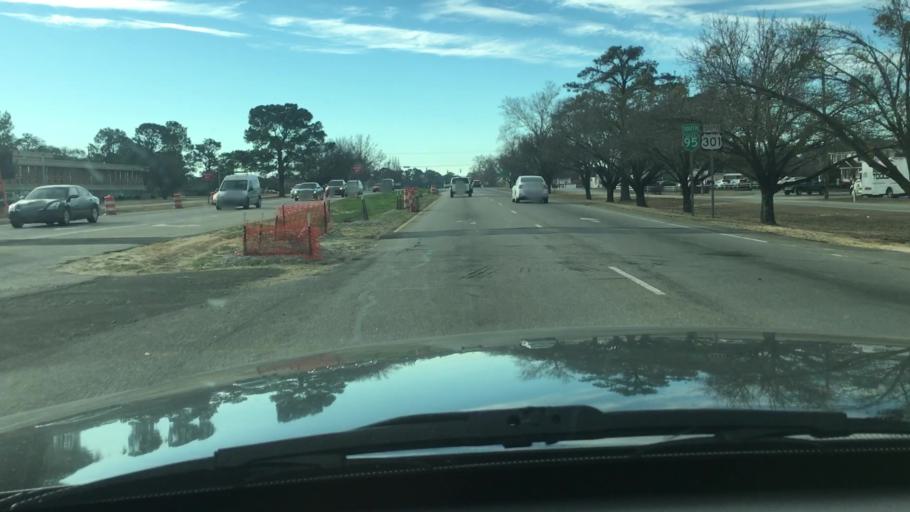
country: US
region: North Carolina
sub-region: Cumberland County
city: Fayetteville
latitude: 35.0154
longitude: -78.8970
